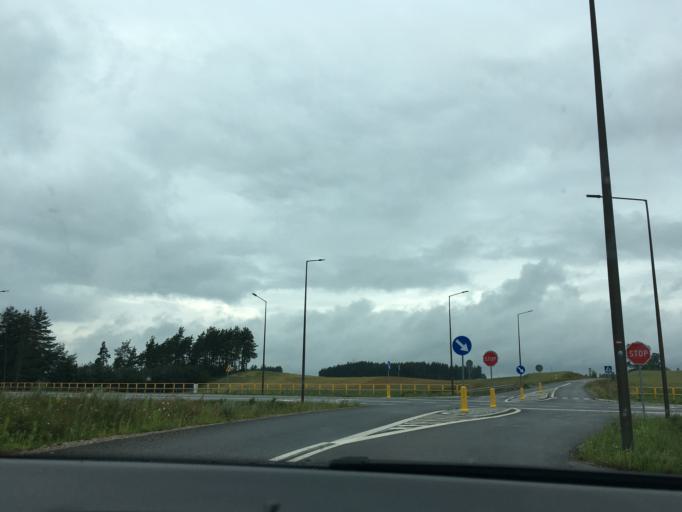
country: PL
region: Podlasie
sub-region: Powiat sejnenski
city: Krasnopol
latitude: 54.0982
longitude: 23.2202
